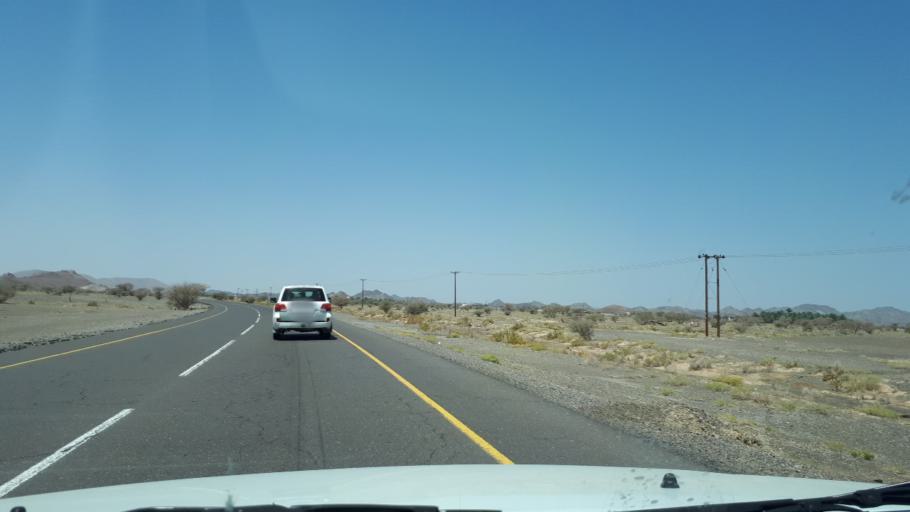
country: OM
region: Ash Sharqiyah
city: Ibra'
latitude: 22.6201
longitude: 58.4061
